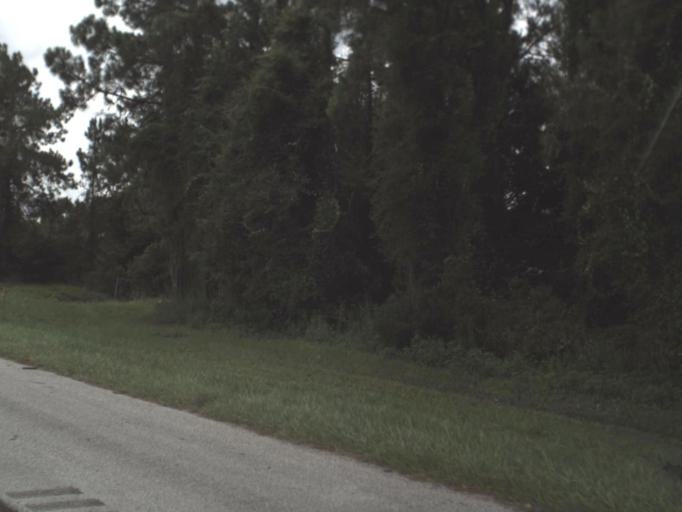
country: US
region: Florida
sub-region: Pasco County
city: San Antonio
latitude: 28.3119
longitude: -82.3257
